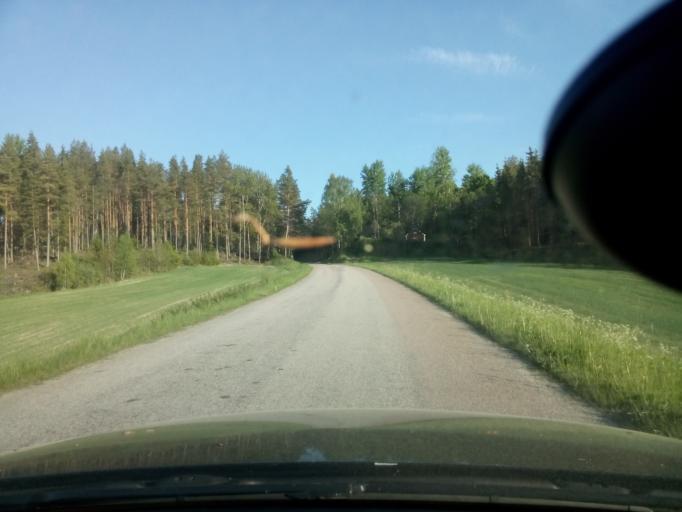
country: SE
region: Soedermanland
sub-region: Nykopings Kommun
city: Nykoping
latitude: 58.8937
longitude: 16.9911
